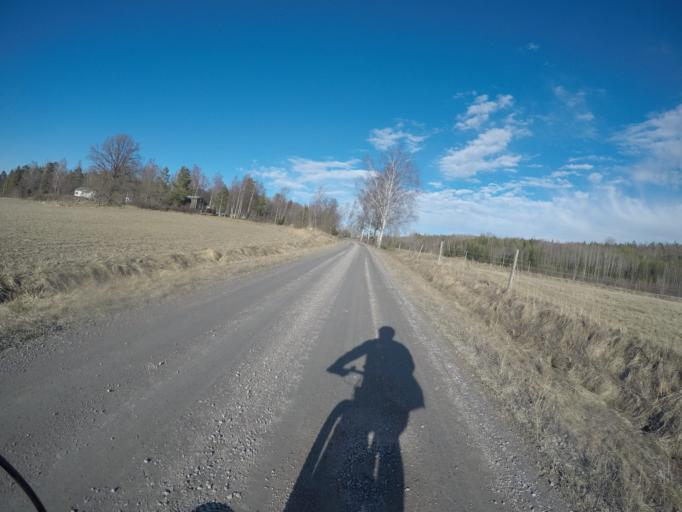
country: SE
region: Soedermanland
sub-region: Eskilstuna Kommun
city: Kvicksund
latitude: 59.4125
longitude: 16.2704
